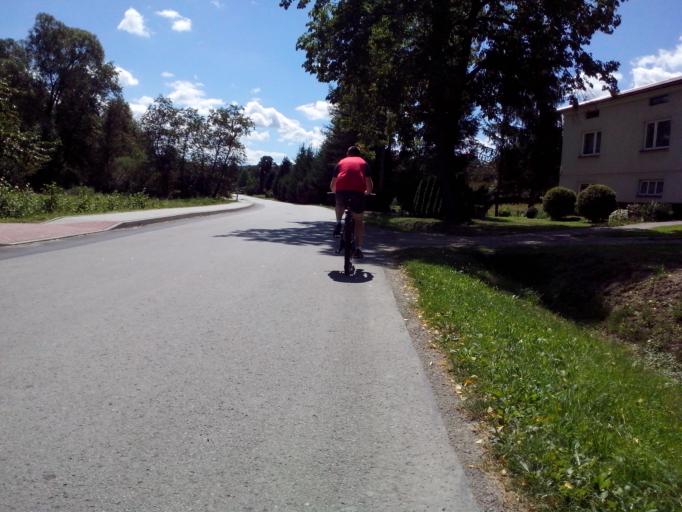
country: PL
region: Subcarpathian Voivodeship
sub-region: Powiat brzozowski
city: Blizne
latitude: 49.7826
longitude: 21.9910
